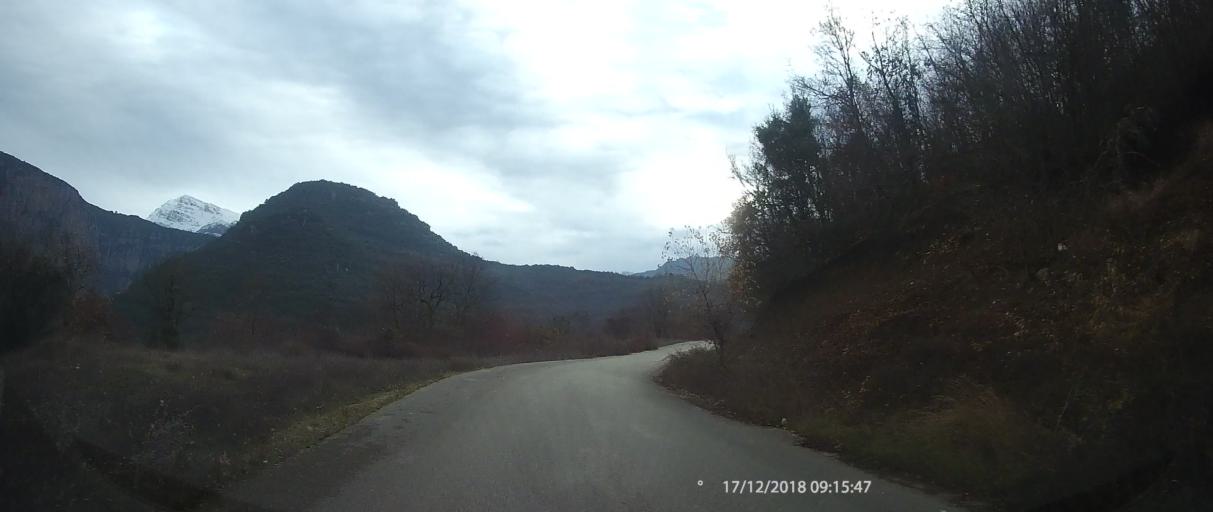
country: GR
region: Epirus
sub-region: Nomos Ioanninon
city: Kalpaki
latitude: 39.9656
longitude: 20.6563
